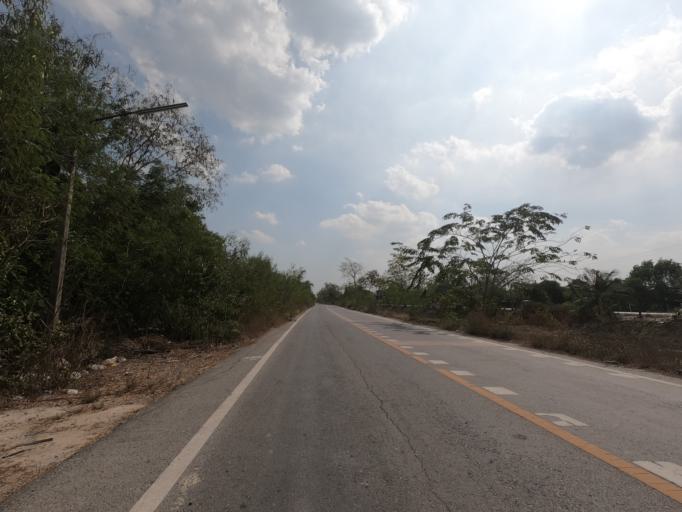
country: TH
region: Pathum Thani
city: Nong Suea
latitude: 14.1653
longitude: 100.8463
